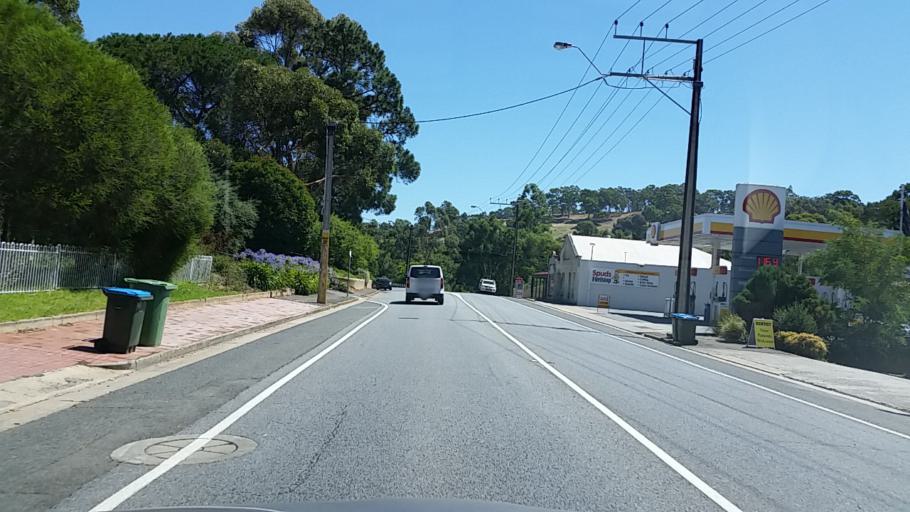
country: AU
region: South Australia
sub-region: Mount Barker
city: Little Hampton
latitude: -35.0495
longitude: 138.8601
